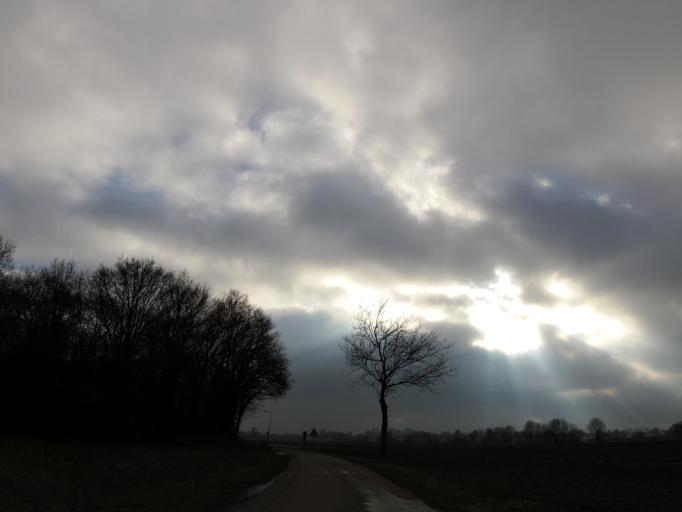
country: NL
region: Limburg
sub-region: Gemeente Bergen
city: Wellerlooi
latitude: 51.5414
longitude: 6.1187
